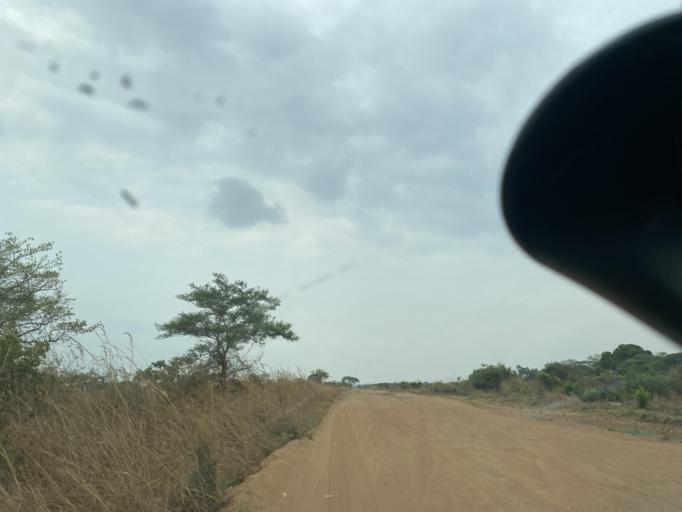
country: ZM
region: Lusaka
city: Lusaka
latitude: -15.2240
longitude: 28.3367
